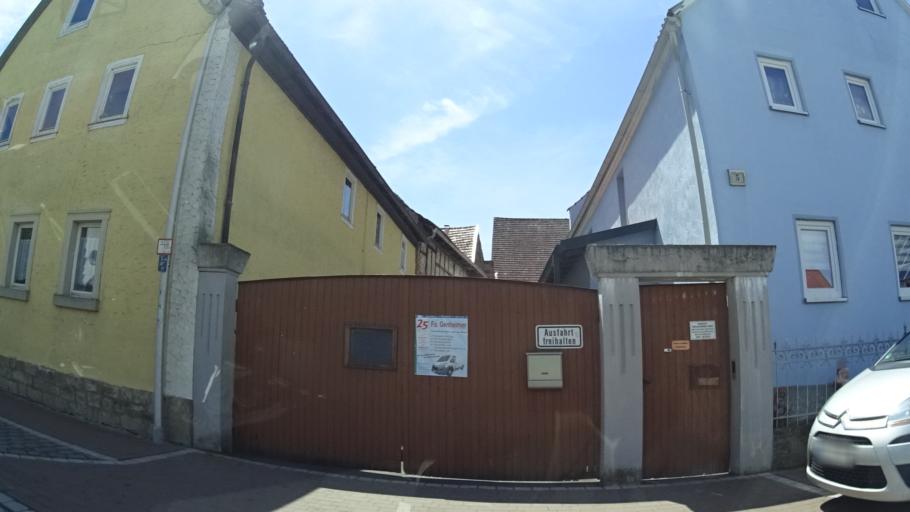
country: DE
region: Bavaria
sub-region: Regierungsbezirk Unterfranken
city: Poppenhausen
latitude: 50.0838
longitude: 10.1450
